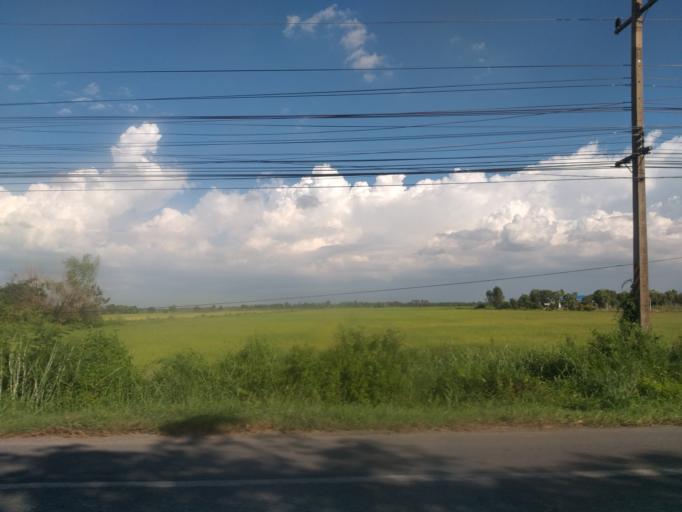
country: TH
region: Nakhon Nayok
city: Ongkharak
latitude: 14.1759
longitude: 101.0264
